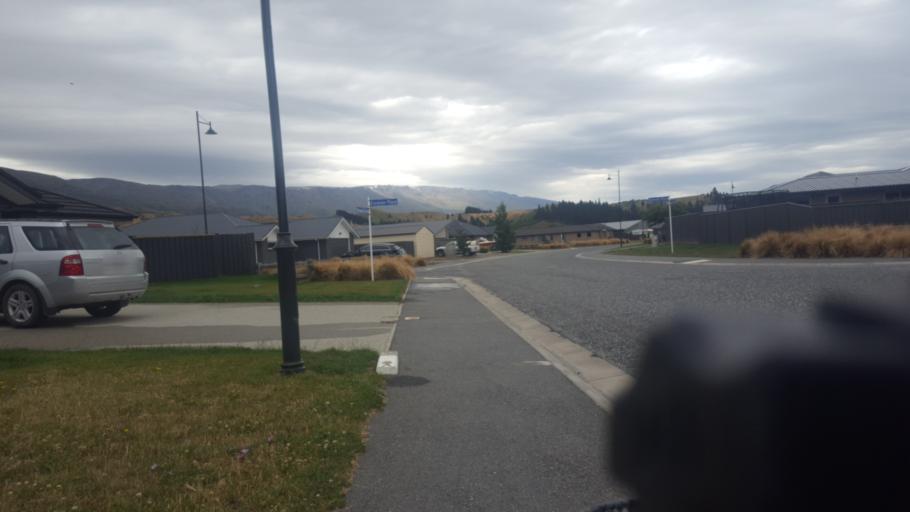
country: NZ
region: Otago
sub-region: Queenstown-Lakes District
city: Wanaka
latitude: -45.0475
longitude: 169.1795
